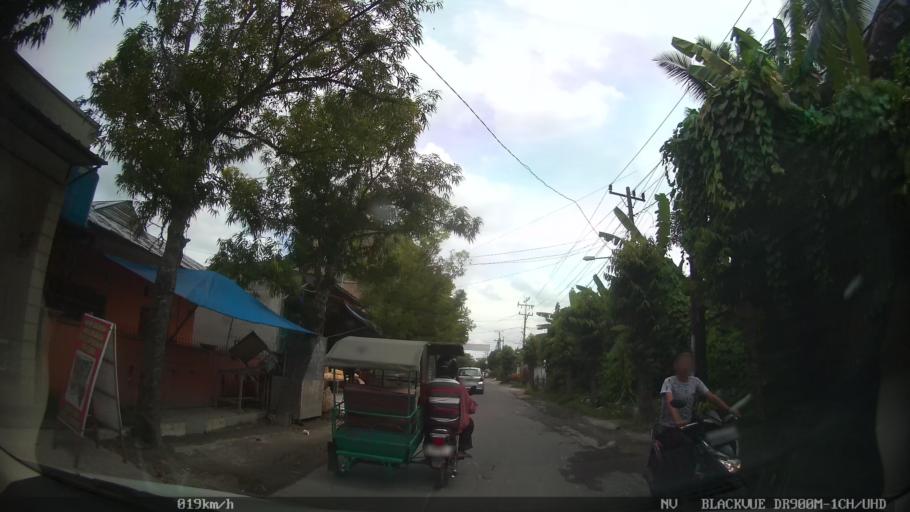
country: ID
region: North Sumatra
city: Percut
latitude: 3.5592
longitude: 98.8673
